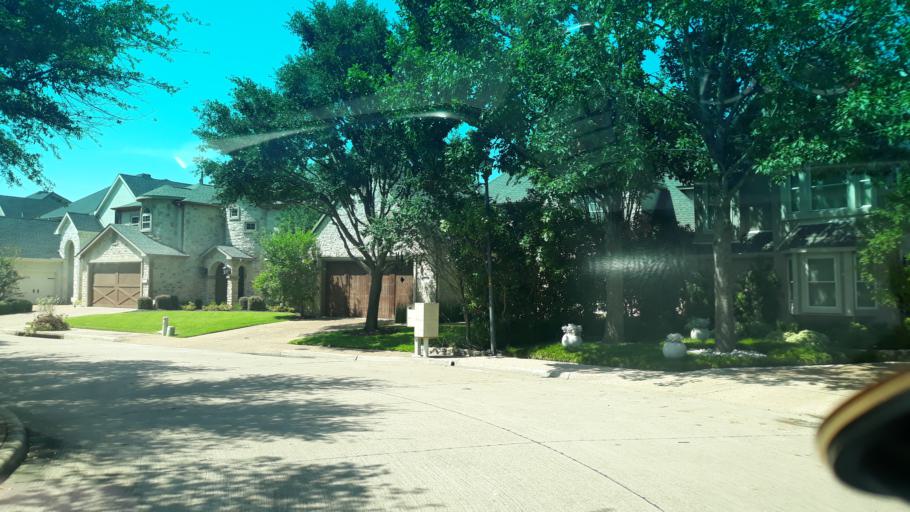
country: US
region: Texas
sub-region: Dallas County
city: Highland Park
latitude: 32.8129
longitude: -96.7247
